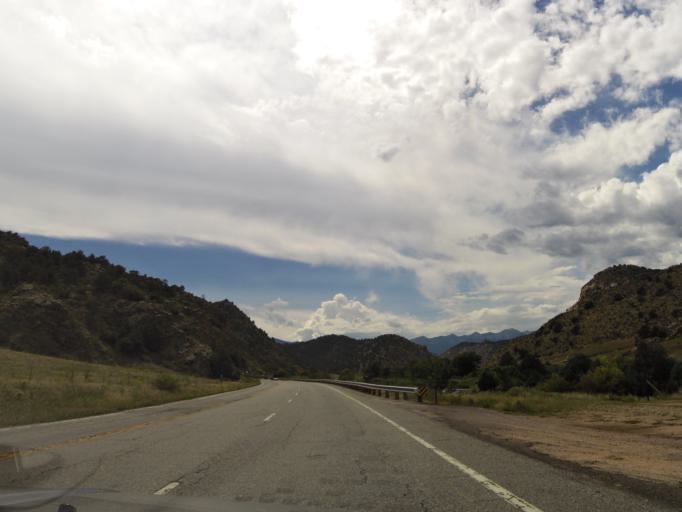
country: US
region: Colorado
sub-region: Custer County
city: Westcliffe
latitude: 38.3955
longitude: -105.6348
